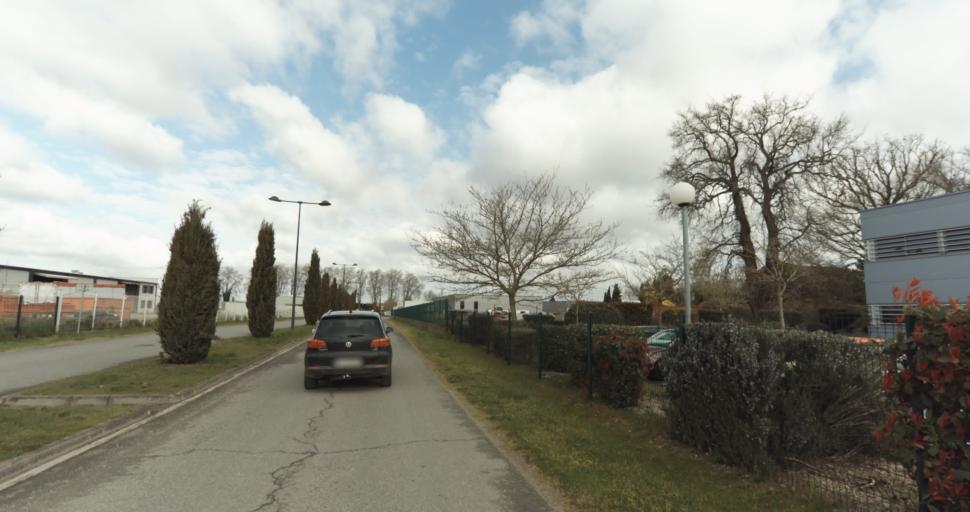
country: FR
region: Midi-Pyrenees
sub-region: Departement de la Haute-Garonne
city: Auterive
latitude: 43.3646
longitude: 1.4523
